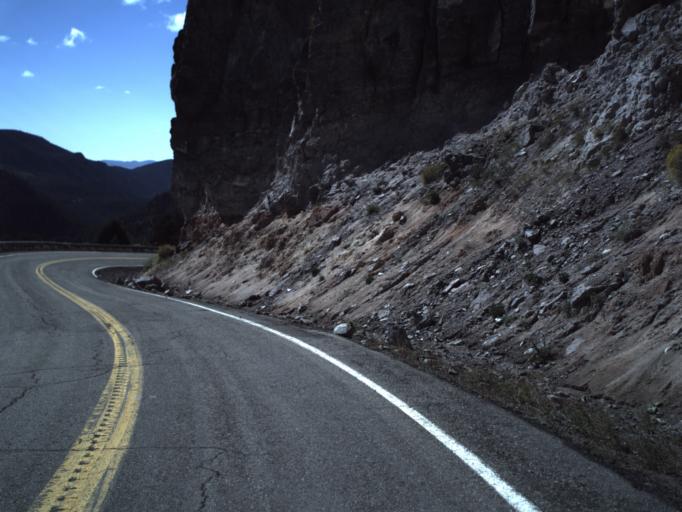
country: US
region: Utah
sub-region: Beaver County
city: Beaver
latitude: 38.2716
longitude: -112.4770
